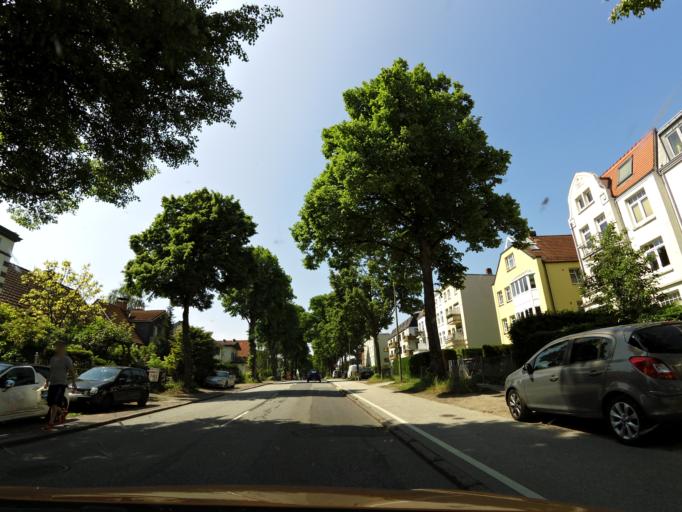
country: DE
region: Schleswig-Holstein
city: Luebeck
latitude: 53.8744
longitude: 10.7164
